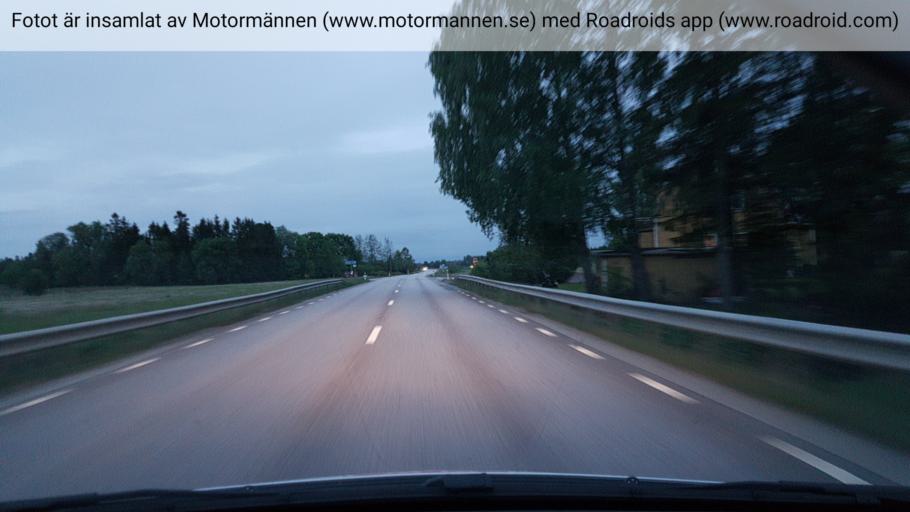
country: SE
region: Vaestmanland
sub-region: Sala Kommun
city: Sala
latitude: 59.8606
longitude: 16.6332
